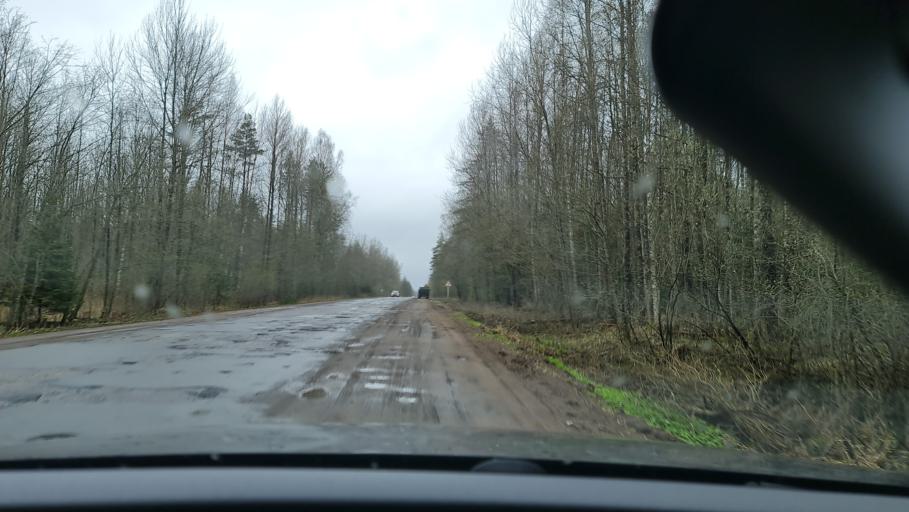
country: RU
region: Novgorod
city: Demyansk
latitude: 57.6735
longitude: 32.5482
